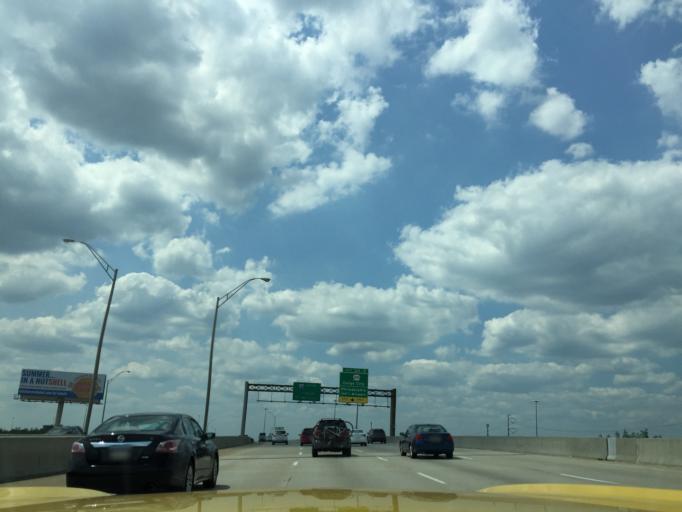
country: US
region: Pennsylvania
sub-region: Delaware County
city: Colwyn
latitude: 39.8908
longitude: -75.2212
